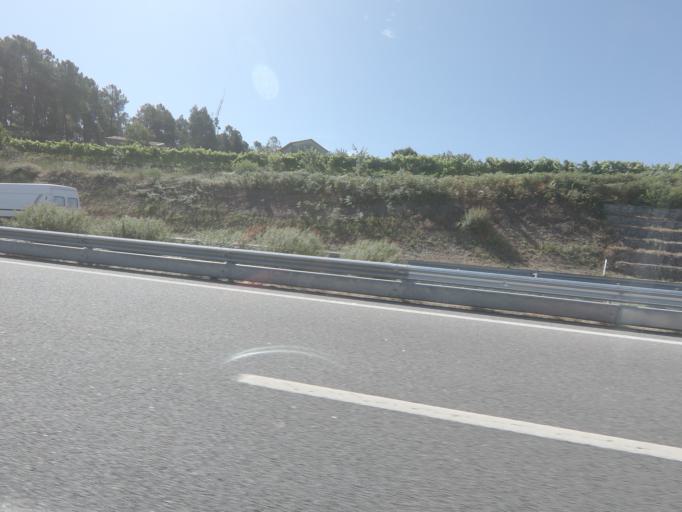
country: PT
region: Porto
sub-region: Lousada
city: Meinedo
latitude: 41.2289
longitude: -8.2276
